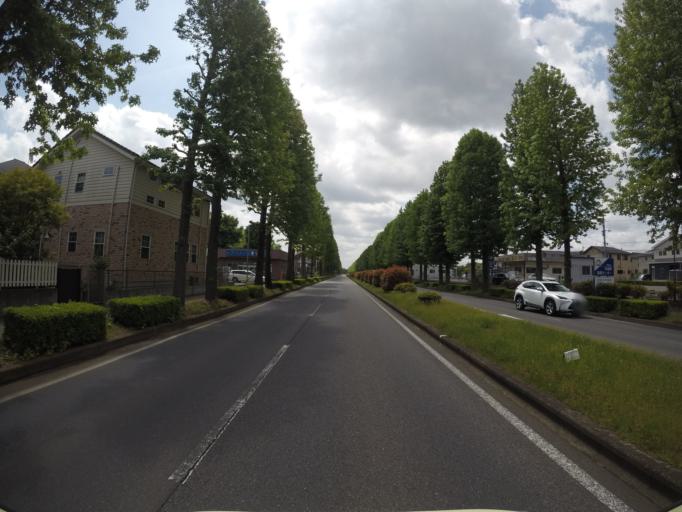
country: JP
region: Ibaraki
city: Naka
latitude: 36.0702
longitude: 140.0985
